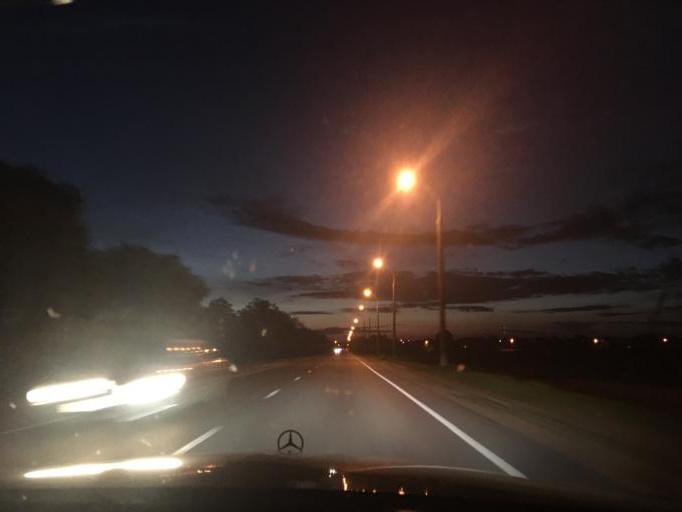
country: BY
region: Brest
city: Brest
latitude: 52.0615
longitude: 23.7008
